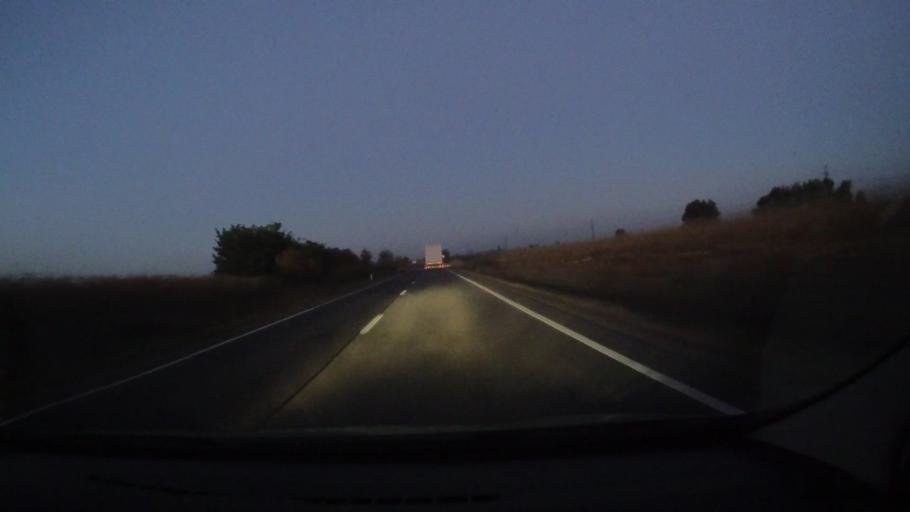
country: RO
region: Bihor
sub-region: Comuna Valea lui Mihai
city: Valea lui Mihai
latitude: 47.5218
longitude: 22.1754
